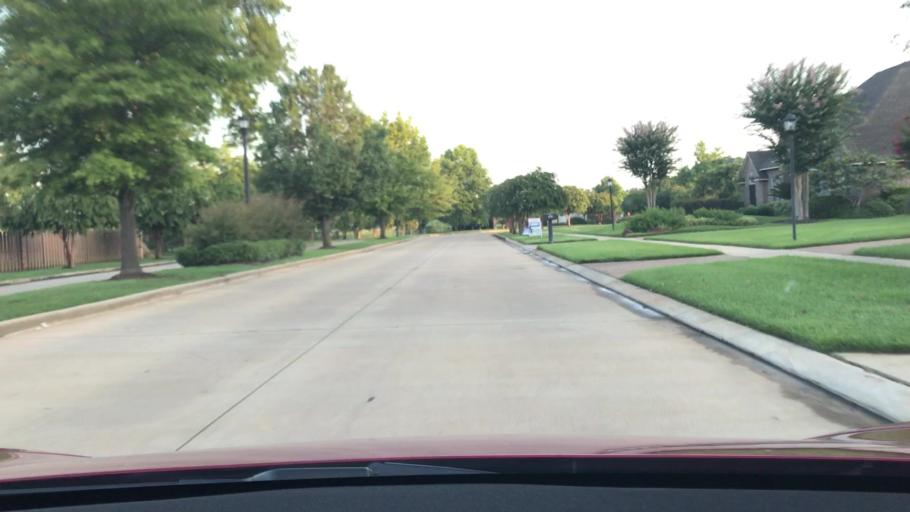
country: US
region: Louisiana
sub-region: Bossier Parish
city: Bossier City
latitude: 32.3986
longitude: -93.7096
